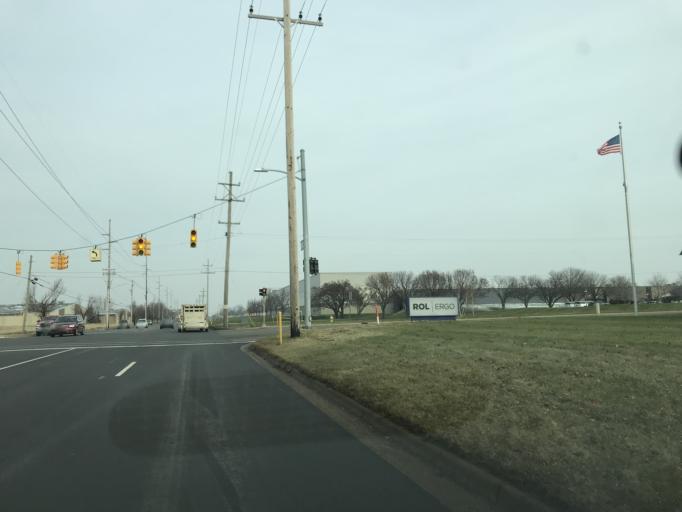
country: US
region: Michigan
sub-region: Ottawa County
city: Holland
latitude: 42.7617
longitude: -86.0773
